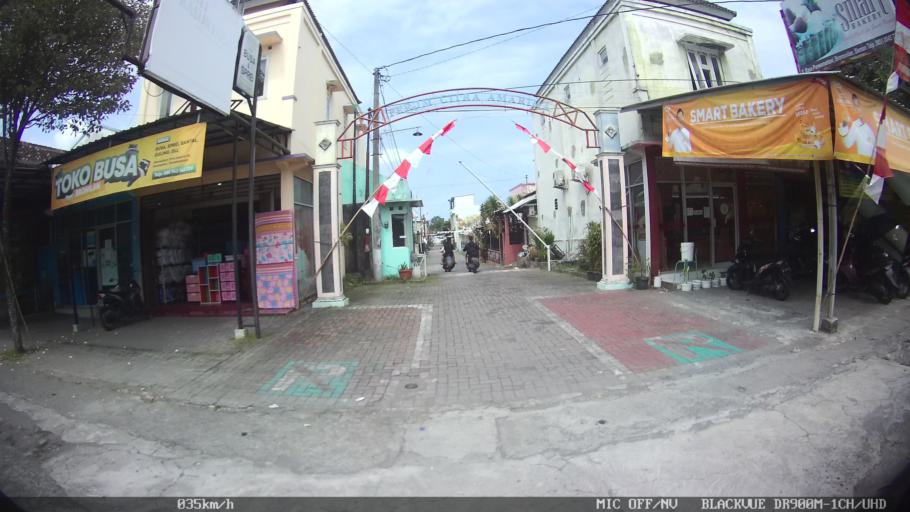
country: ID
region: Daerah Istimewa Yogyakarta
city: Depok
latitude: -7.7428
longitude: 110.4510
